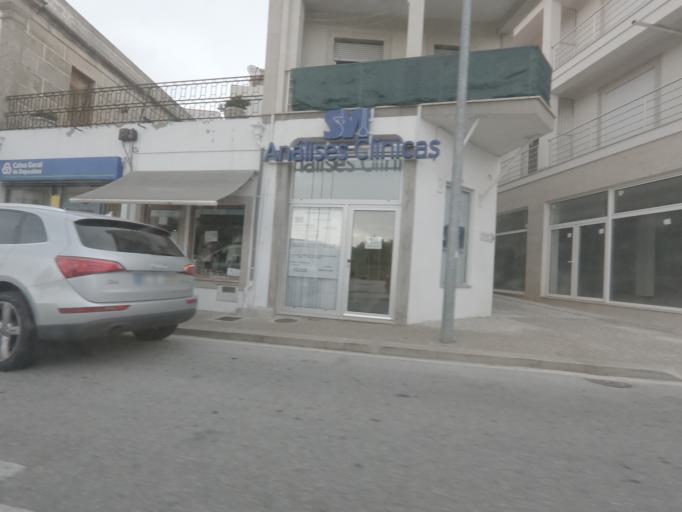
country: PT
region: Viseu
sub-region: Armamar
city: Armamar
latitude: 41.1083
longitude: -7.6932
